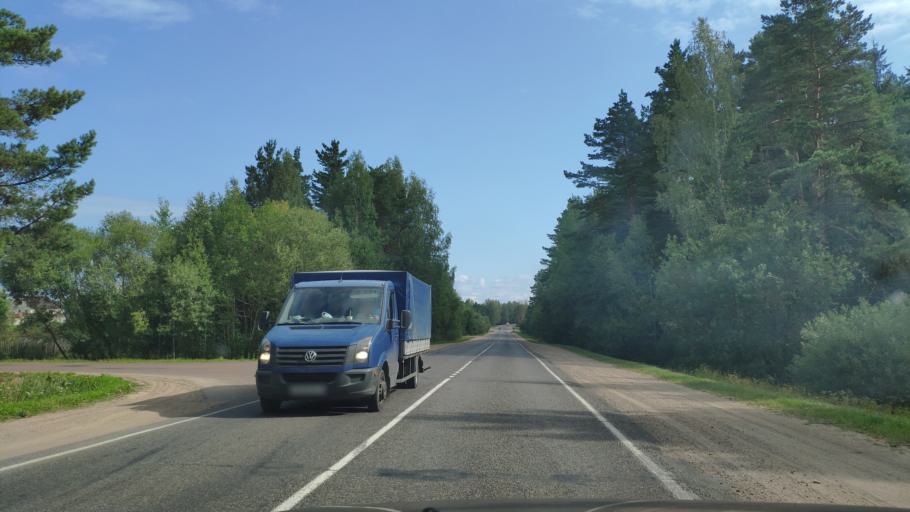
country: BY
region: Minsk
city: Zaslawye
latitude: 53.9822
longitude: 27.2542
